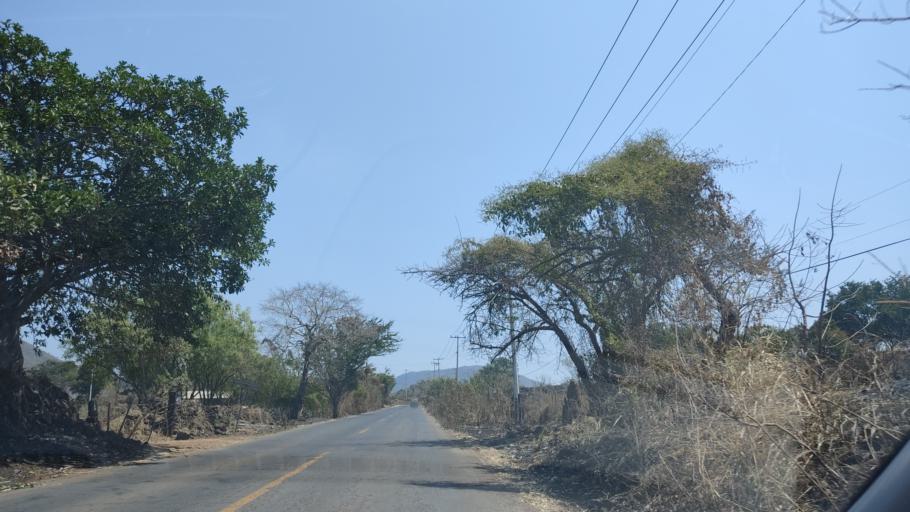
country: MX
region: Nayarit
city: Puga
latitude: 21.5880
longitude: -104.8060
